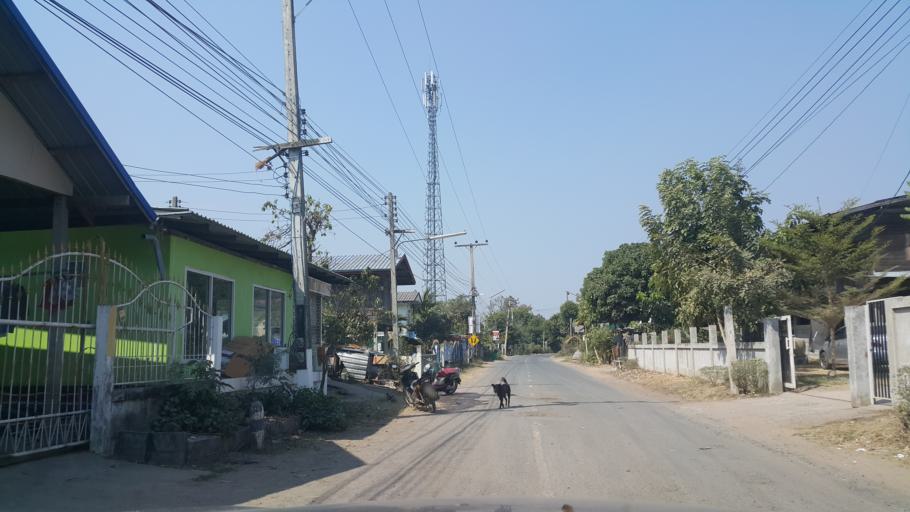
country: TH
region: Buriram
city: Satuek
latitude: 15.1313
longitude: 103.3759
